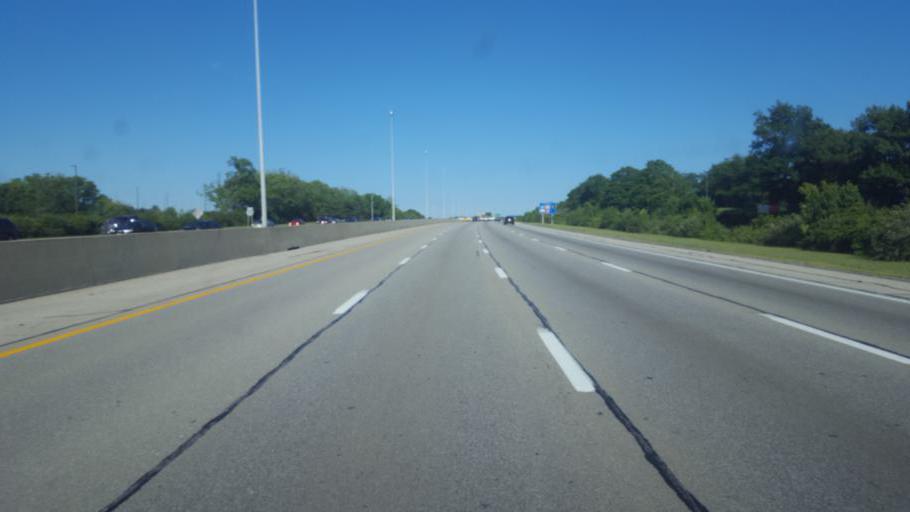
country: US
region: Ohio
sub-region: Franklin County
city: Dublin
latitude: 40.1094
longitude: -83.1026
